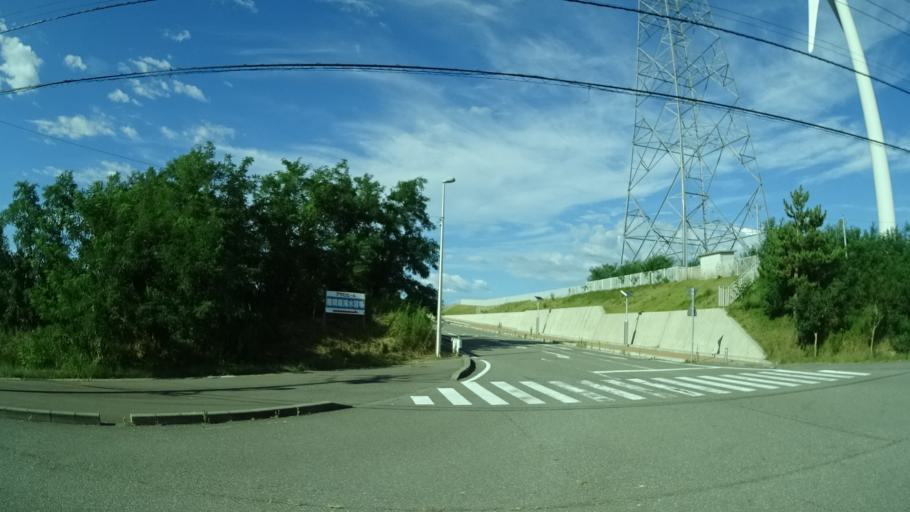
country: JP
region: Ishikawa
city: Kanazawa-shi
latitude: 36.6637
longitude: 136.6489
